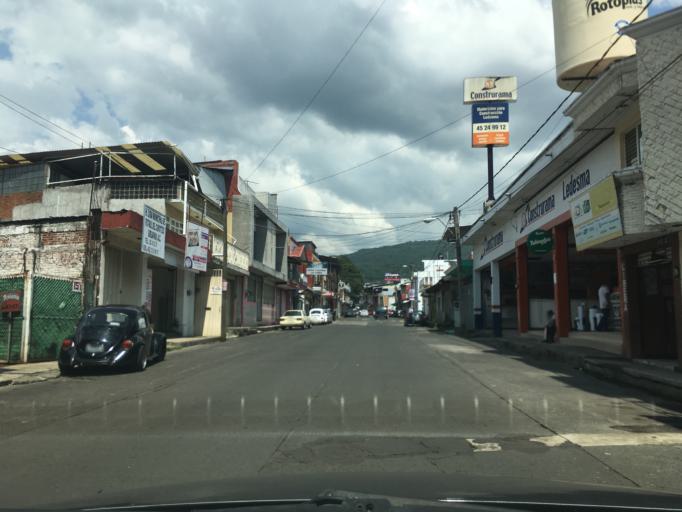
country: MX
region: Michoacan
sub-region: Uruapan
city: Uruapan
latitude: 19.4231
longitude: -102.0546
